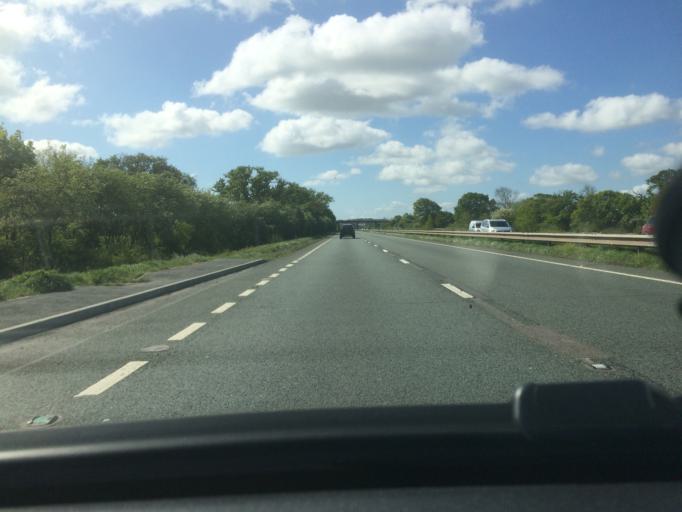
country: GB
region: Wales
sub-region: Wrexham
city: Rossett
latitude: 53.1245
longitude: -2.9491
